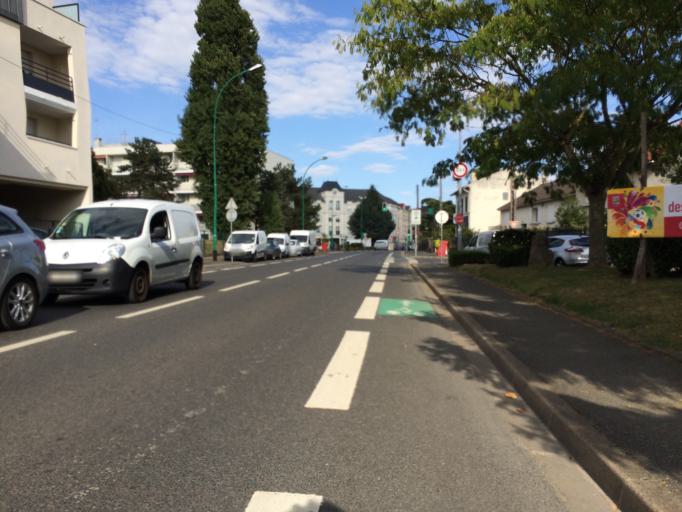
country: FR
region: Ile-de-France
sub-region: Departement de l'Essonne
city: Morangis
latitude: 48.7066
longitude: 2.3269
